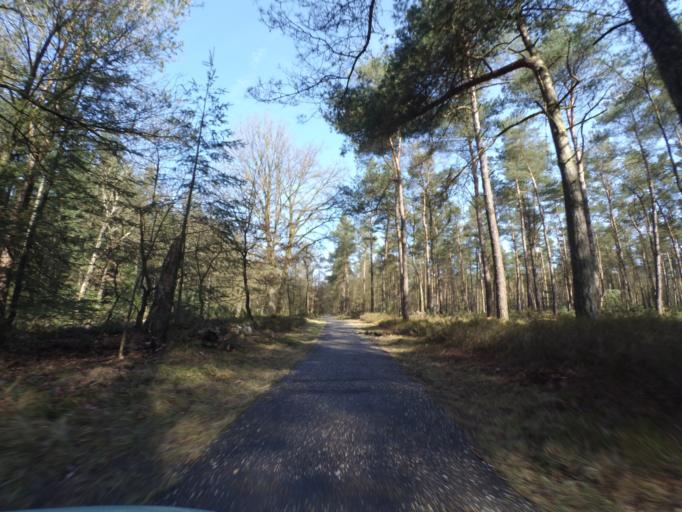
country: NL
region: Gelderland
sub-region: Gemeente Apeldoorn
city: Uddel
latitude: 52.2065
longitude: 5.8098
